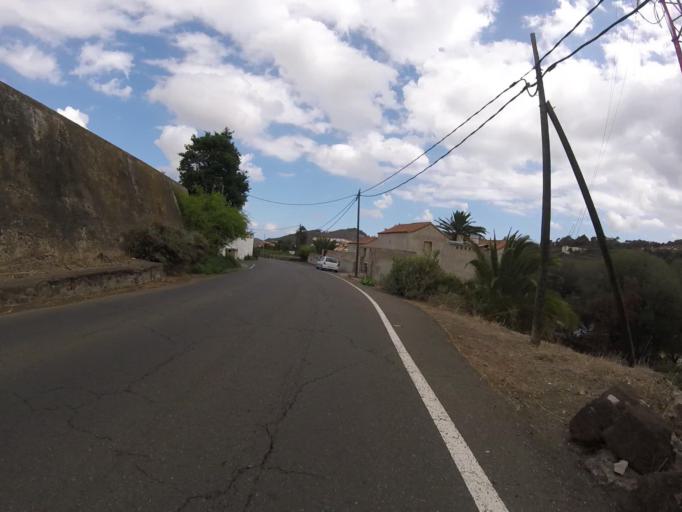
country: ES
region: Canary Islands
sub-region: Provincia de Las Palmas
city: Santa Brigida
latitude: 28.0450
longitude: -15.4854
